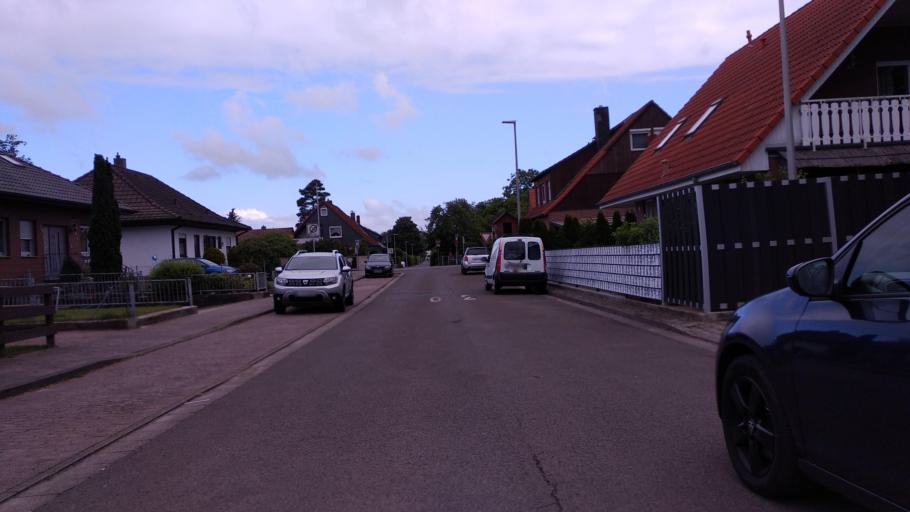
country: DE
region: Lower Saxony
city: Hagenburg
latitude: 52.4552
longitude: 9.3752
